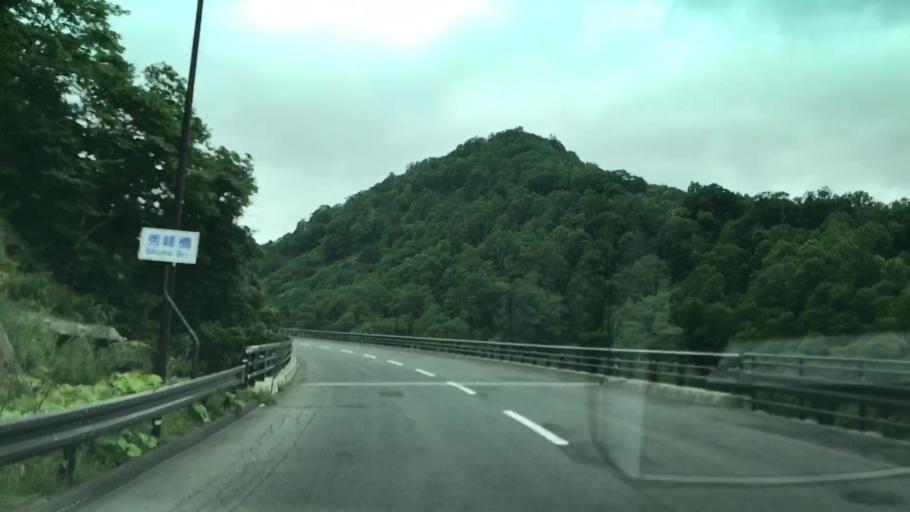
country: JP
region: Hokkaido
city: Yoichi
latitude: 42.9877
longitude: 140.8723
